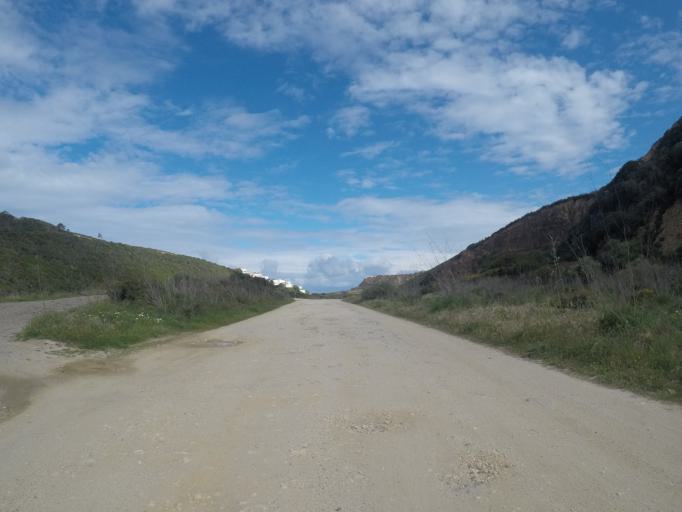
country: PT
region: Beja
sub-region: Odemira
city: Sao Teotonio
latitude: 37.4378
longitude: -8.7925
